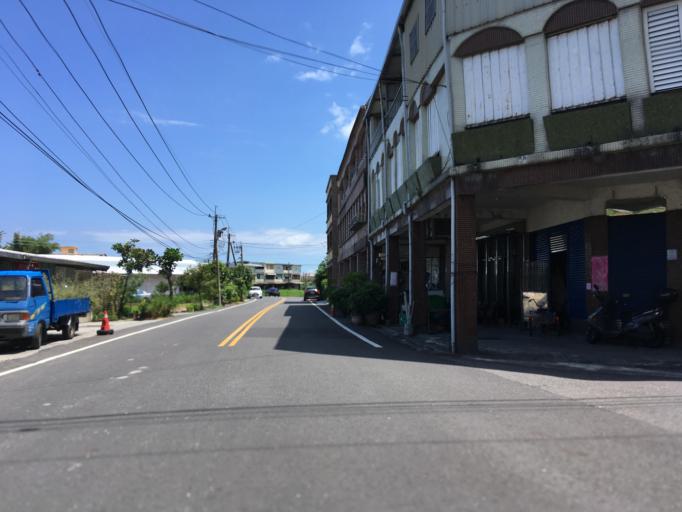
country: TW
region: Taiwan
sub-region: Yilan
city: Yilan
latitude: 24.6858
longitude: 121.8017
